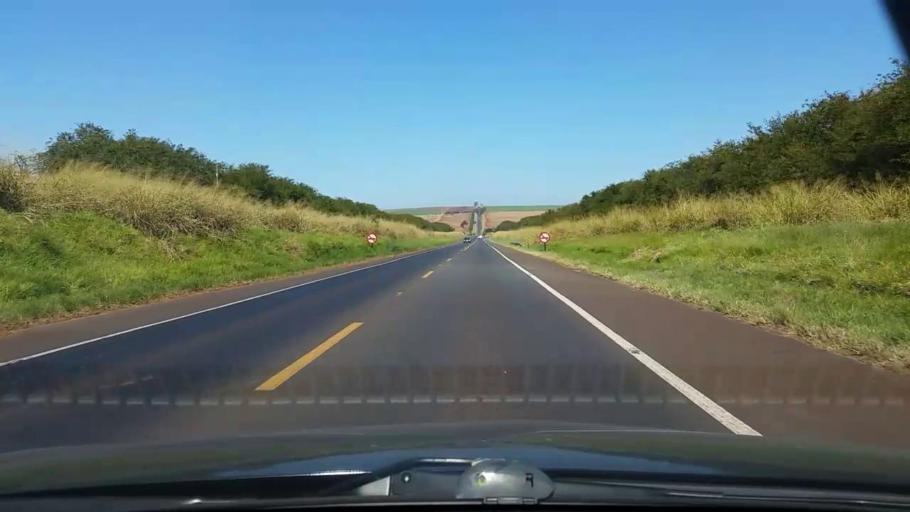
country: BR
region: Sao Paulo
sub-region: Jau
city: Jau
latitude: -22.3636
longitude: -48.5715
